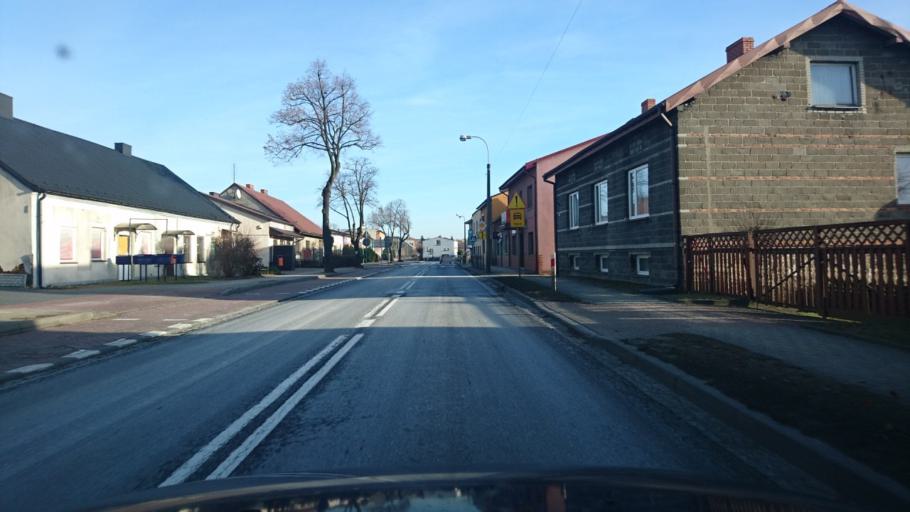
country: PL
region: Opole Voivodeship
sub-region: Powiat oleski
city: Dalachow
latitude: 51.0381
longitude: 18.5998
